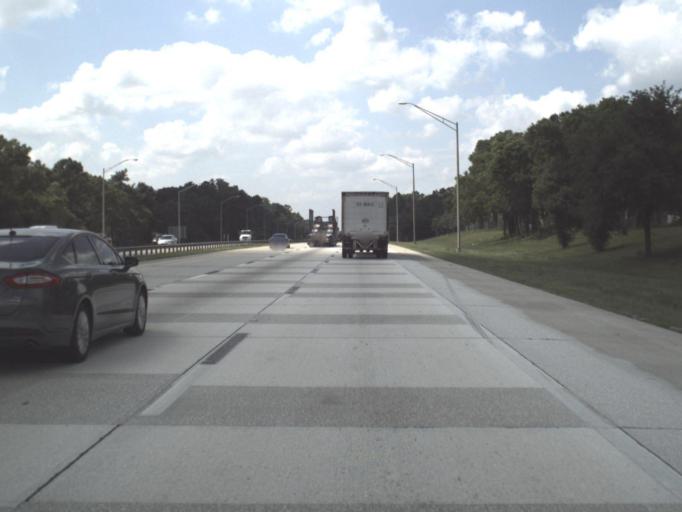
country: US
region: Florida
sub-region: Saint Johns County
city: Fruit Cove
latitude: 30.2030
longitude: -81.5594
